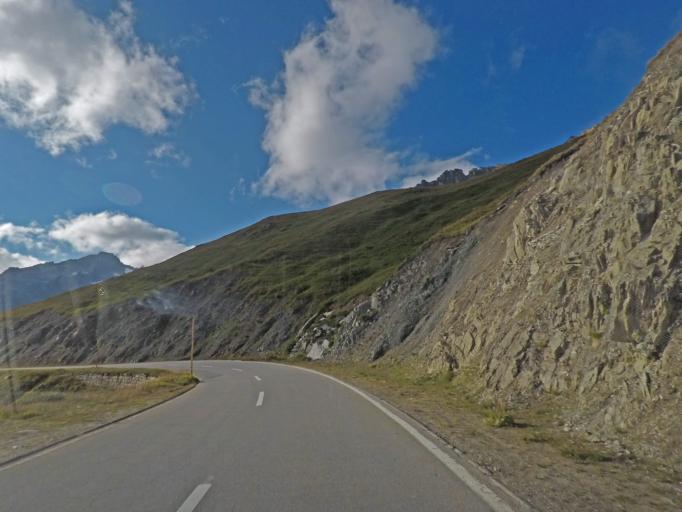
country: IT
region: Piedmont
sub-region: Provincia Verbano-Cusio-Ossola
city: Formazza
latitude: 46.5742
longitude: 8.4045
